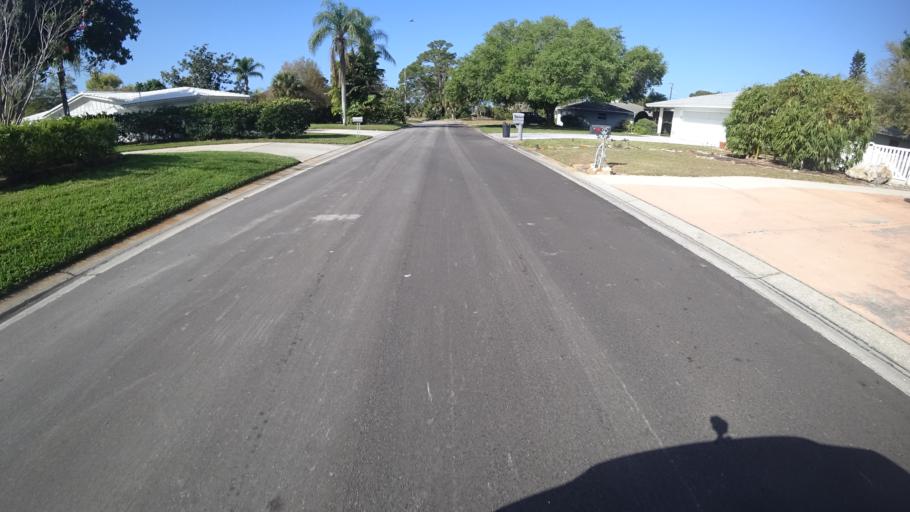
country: US
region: Florida
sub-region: Manatee County
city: Whitfield
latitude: 27.4155
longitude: -82.5704
